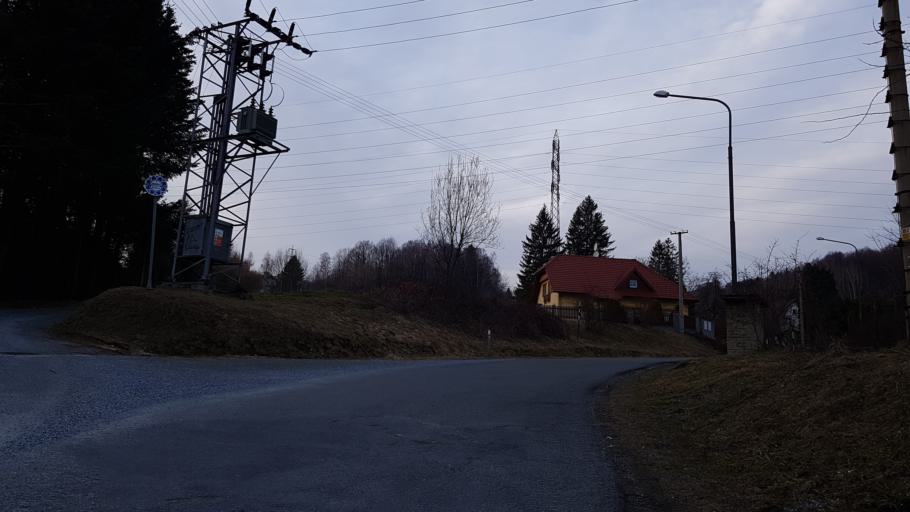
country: CZ
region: Olomoucky
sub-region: Okres Jesenik
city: Jesenik
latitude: 50.2299
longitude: 17.1858
